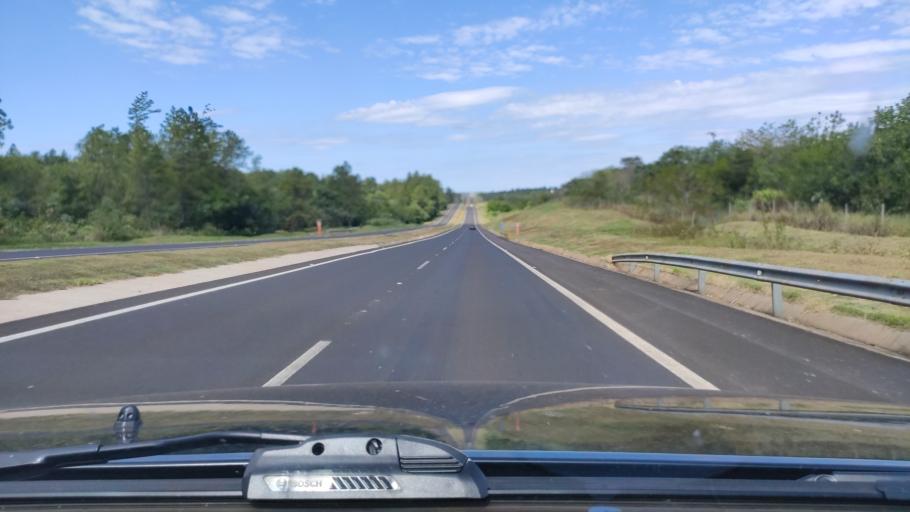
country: BR
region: Sao Paulo
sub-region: Rancharia
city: Rancharia
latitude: -22.4695
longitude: -50.9496
